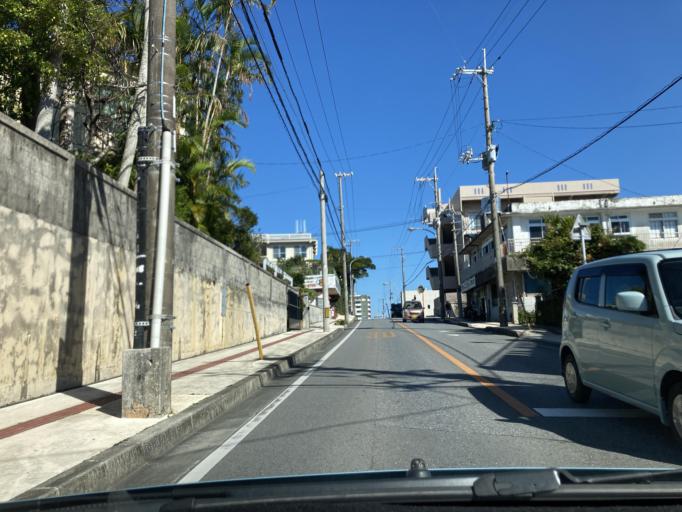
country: JP
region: Okinawa
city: Okinawa
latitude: 26.3295
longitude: 127.8039
